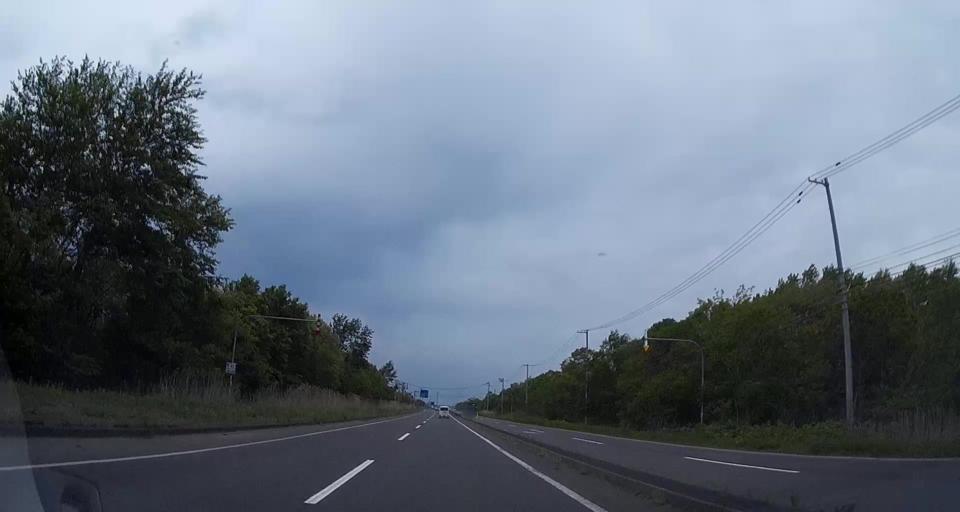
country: JP
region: Hokkaido
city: Tomakomai
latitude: 42.6833
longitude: 141.7197
